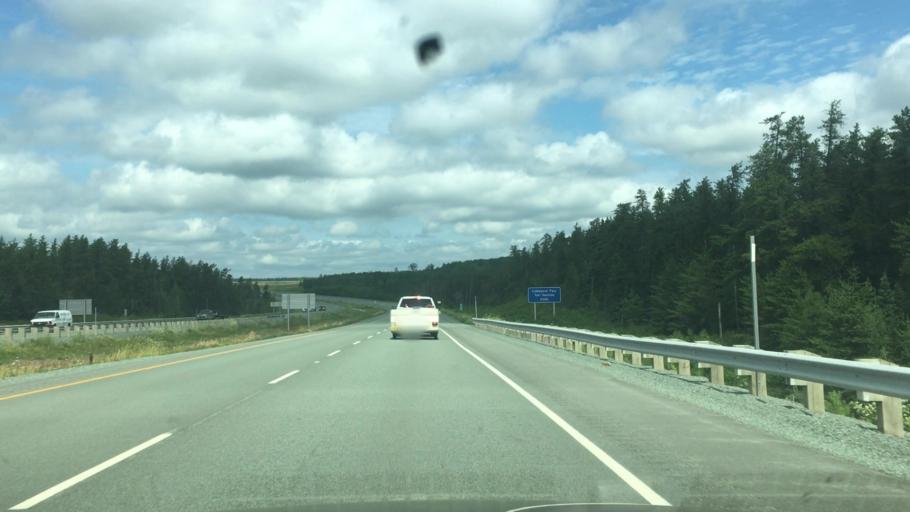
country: CA
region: Nova Scotia
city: Oxford
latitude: 45.6831
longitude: -63.7642
